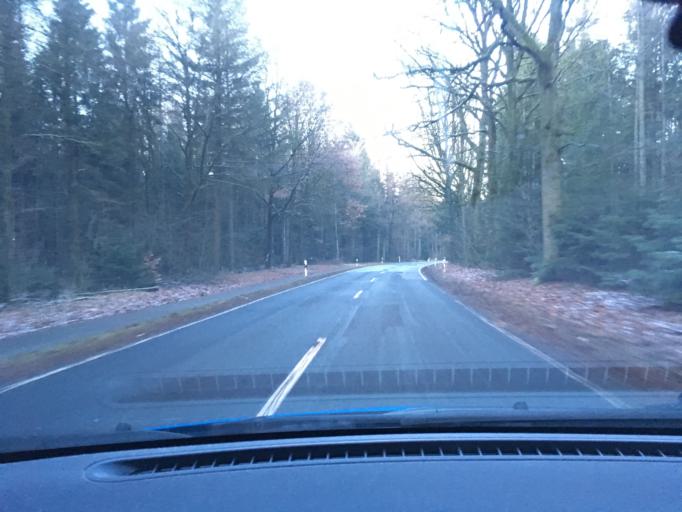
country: DE
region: Lower Saxony
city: Handeloh
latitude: 53.2488
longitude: 9.8745
